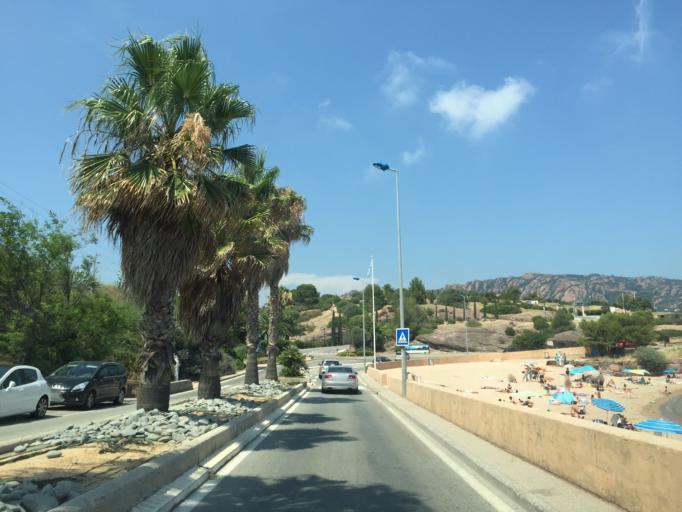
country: FR
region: Provence-Alpes-Cote d'Azur
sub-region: Departement du Var
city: Saint-Raphael
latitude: 43.4249
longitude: 6.8559
